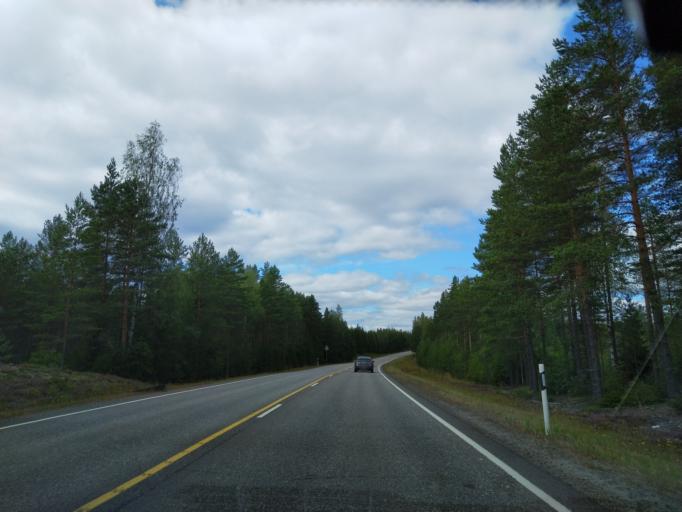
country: FI
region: Haeme
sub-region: Riihimaeki
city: Loppi
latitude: 60.7440
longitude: 24.3528
